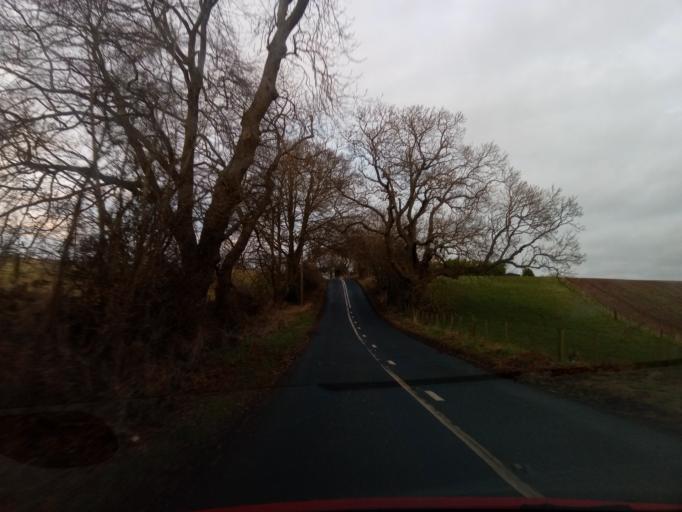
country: GB
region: England
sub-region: Northumberland
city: Meldon
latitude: 55.1236
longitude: -1.7524
